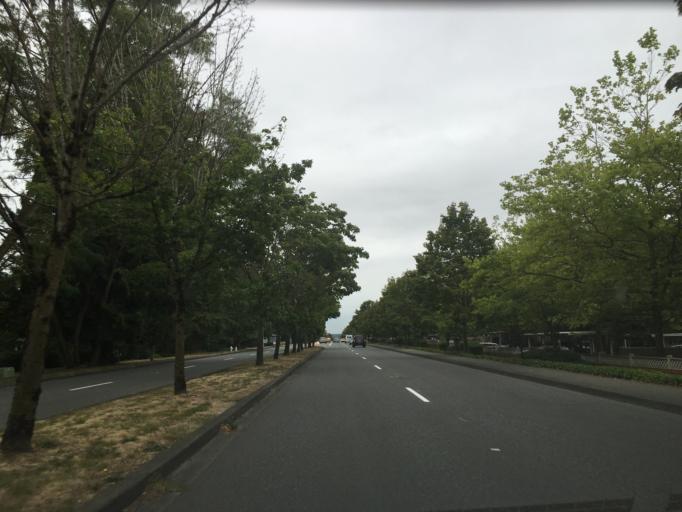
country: US
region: Washington
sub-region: King County
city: Kingsgate
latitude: 47.7112
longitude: -122.1956
